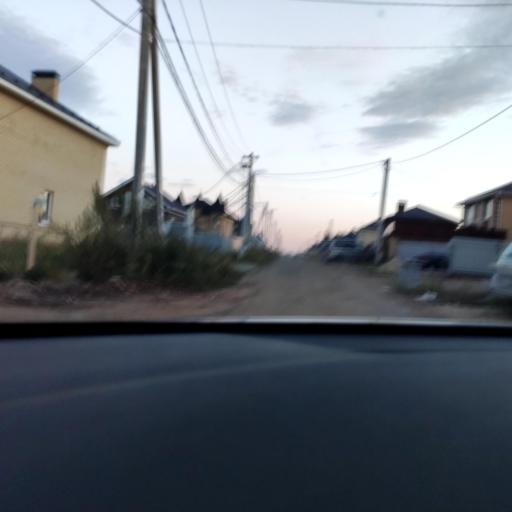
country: RU
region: Tatarstan
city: Stolbishchi
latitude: 55.7224
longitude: 49.3003
